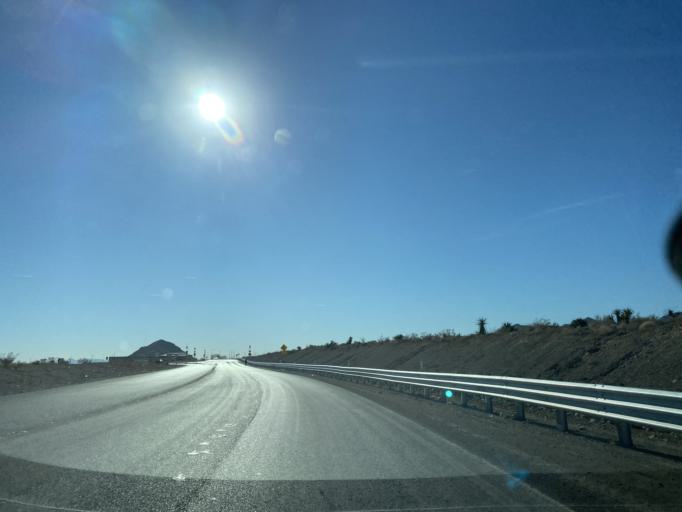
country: US
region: Nevada
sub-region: Clark County
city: Summerlin South
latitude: 36.2623
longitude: -115.3304
